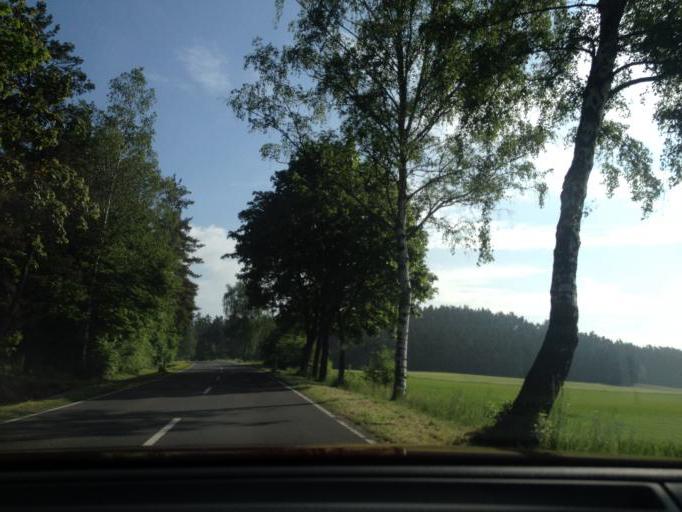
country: DE
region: Bavaria
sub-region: Upper Palatinate
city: Speinshart
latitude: 49.7910
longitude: 11.8328
